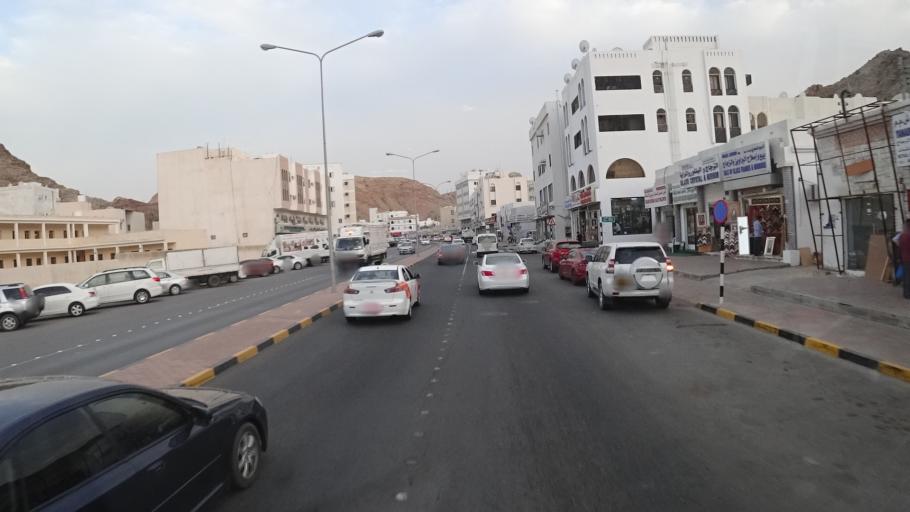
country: OM
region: Muhafazat Masqat
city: Muscat
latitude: 23.5834
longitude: 58.5408
